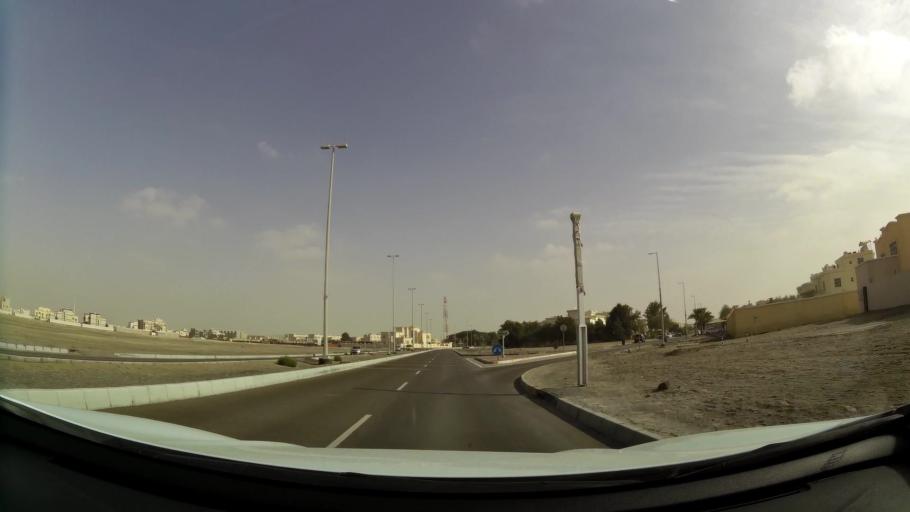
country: AE
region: Abu Dhabi
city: Abu Dhabi
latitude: 24.4168
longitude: 54.6003
